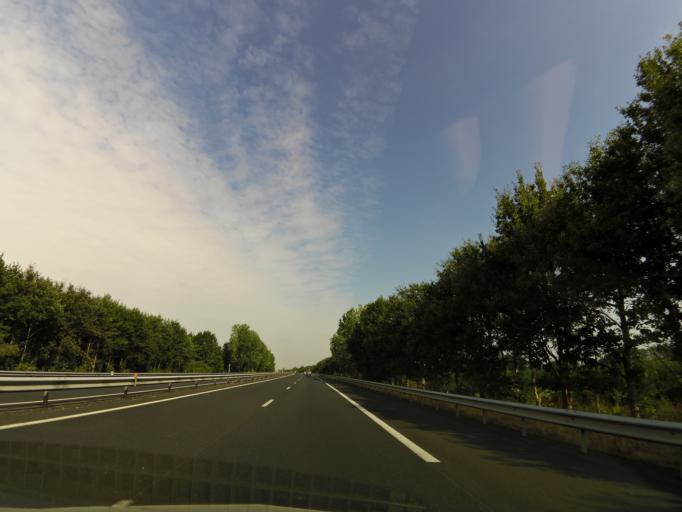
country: FR
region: Pays de la Loire
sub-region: Departement de la Vendee
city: Les Brouzils
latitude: 46.8937
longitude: -1.2983
